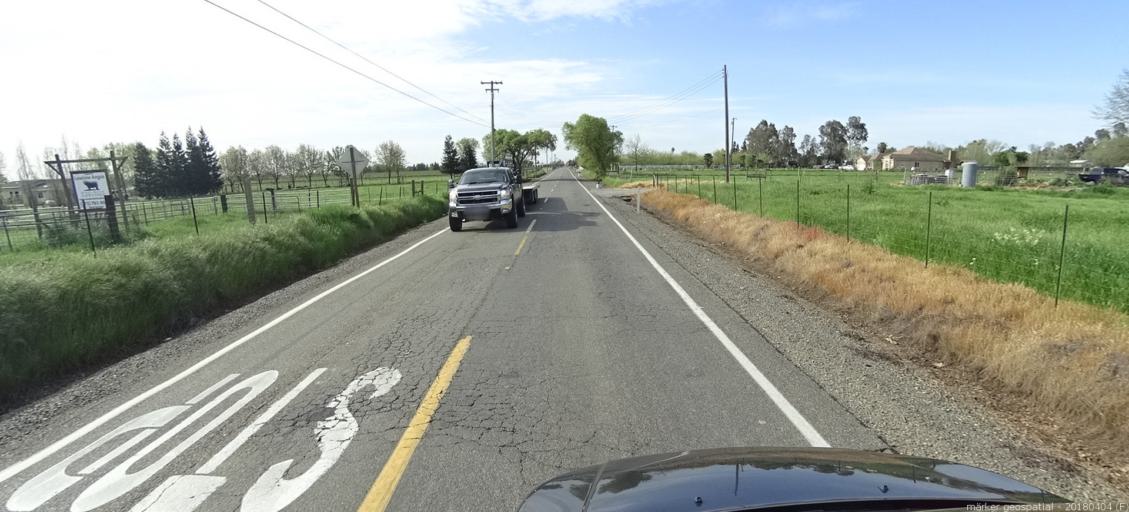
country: US
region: California
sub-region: Sacramento County
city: Herald
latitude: 38.2903
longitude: -121.2265
